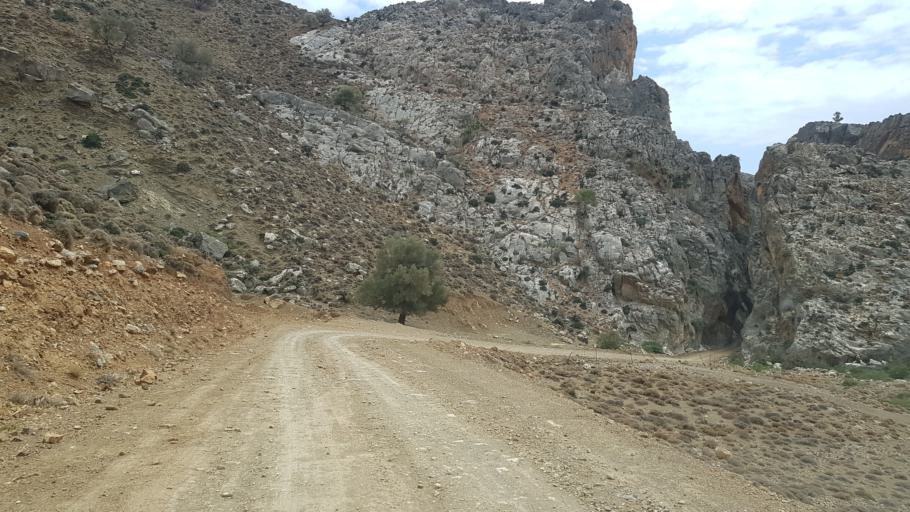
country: GR
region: Crete
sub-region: Nomos Irakleiou
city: Agioi Deka
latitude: 34.9442
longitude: 24.9856
